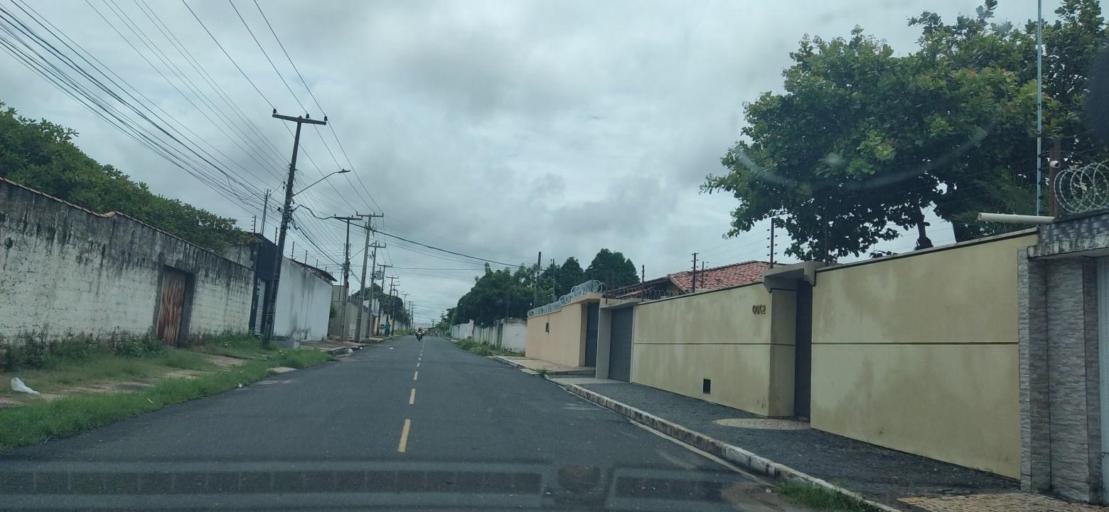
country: BR
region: Piaui
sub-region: Teresina
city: Teresina
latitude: -5.0717
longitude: -42.7648
